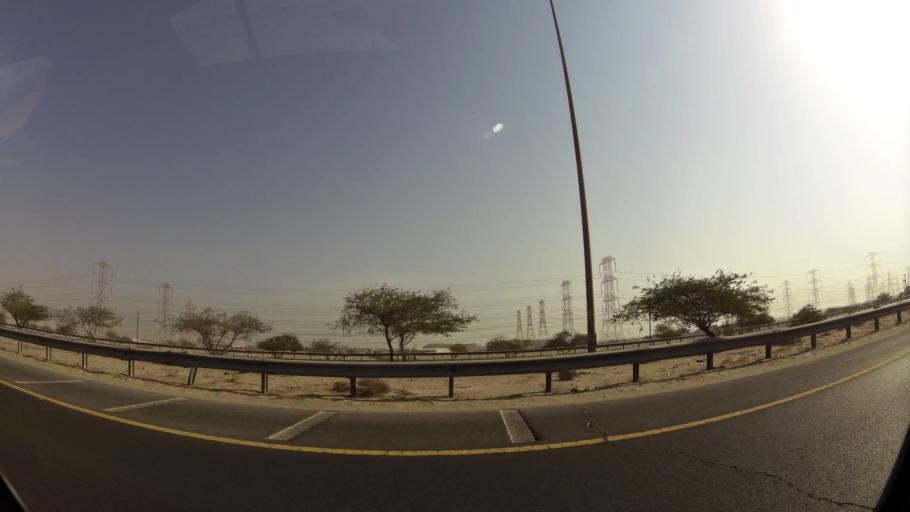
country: KW
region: Al Ahmadi
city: Al Ahmadi
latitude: 28.9691
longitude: 48.1147
